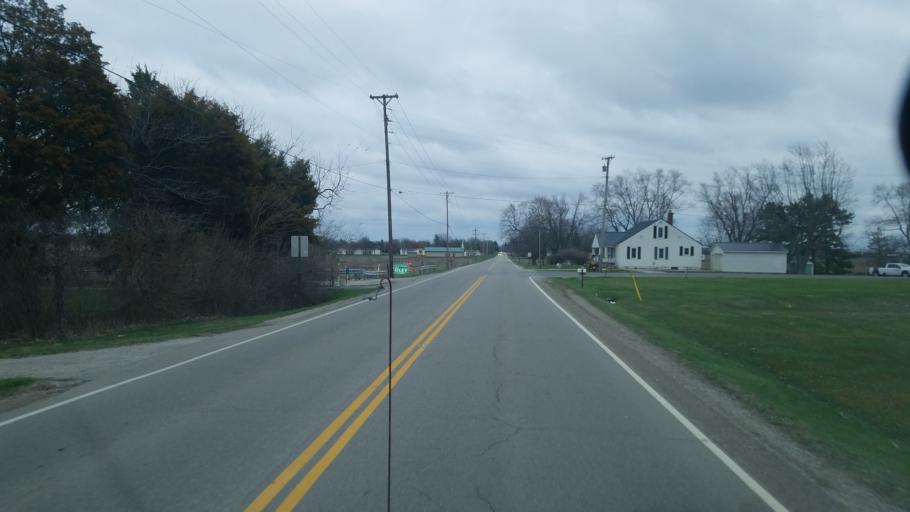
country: US
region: Ohio
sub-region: Fayette County
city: Washington Court House
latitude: 39.5445
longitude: -83.4689
